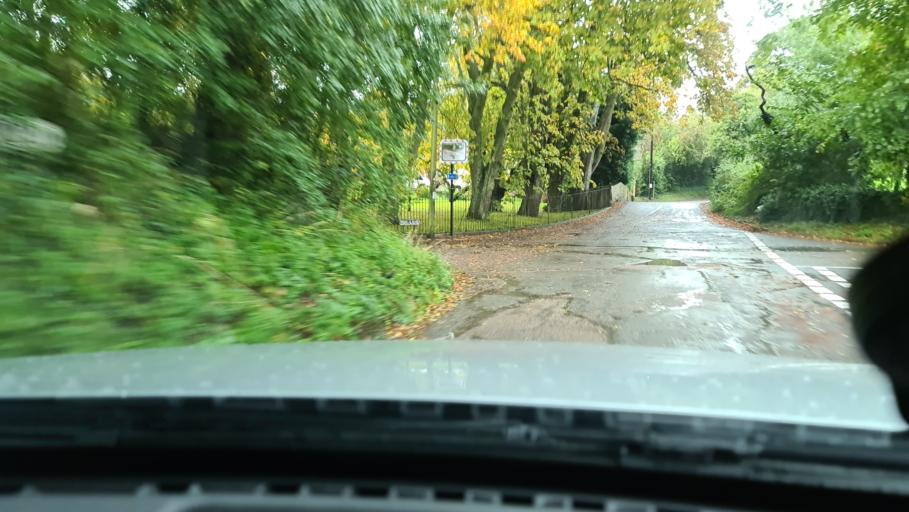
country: GB
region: England
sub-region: Oxfordshire
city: Deddington
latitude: 51.9269
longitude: -1.3686
